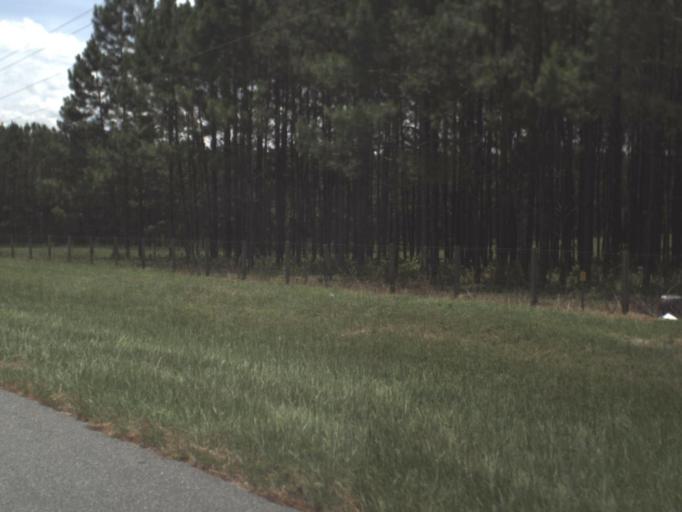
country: US
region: Florida
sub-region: Alachua County
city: High Springs
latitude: 30.0039
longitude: -82.5880
